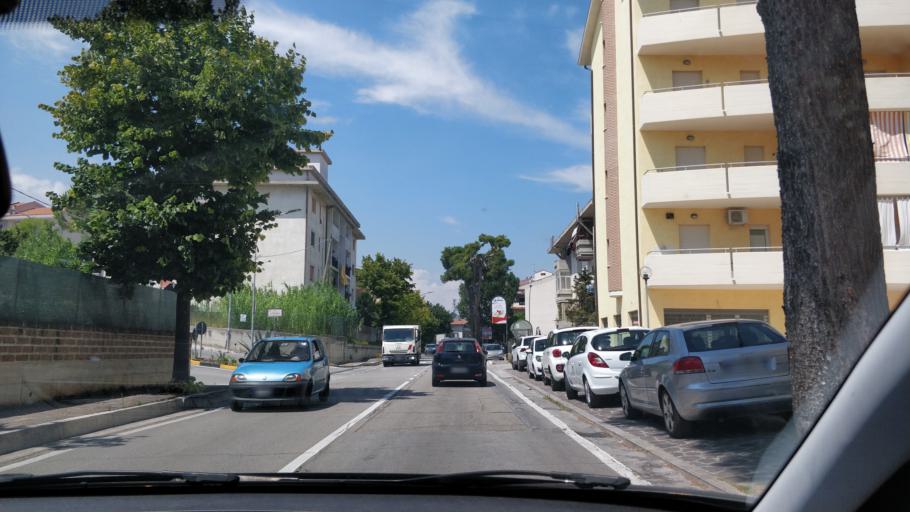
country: IT
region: Abruzzo
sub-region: Provincia di Chieti
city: Francavilla al Mare
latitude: 42.4074
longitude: 14.3094
